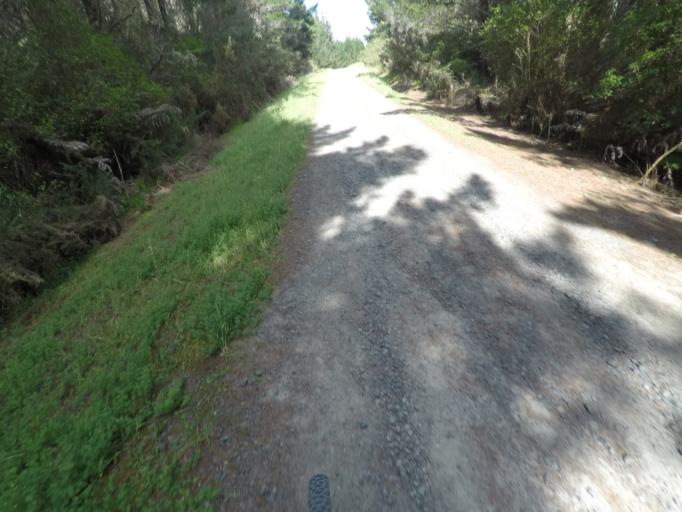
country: NZ
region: Auckland
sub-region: Auckland
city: Muriwai Beach
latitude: -36.7434
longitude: 174.5696
